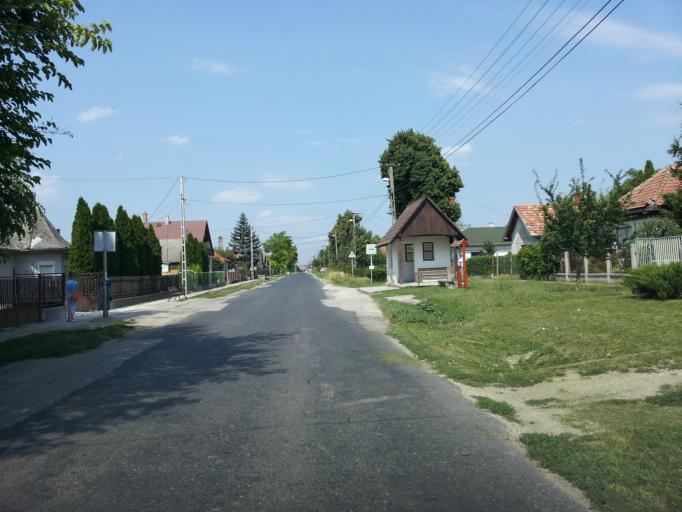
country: HU
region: Veszprem
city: Balatonkenese
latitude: 47.0784
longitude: 18.0769
